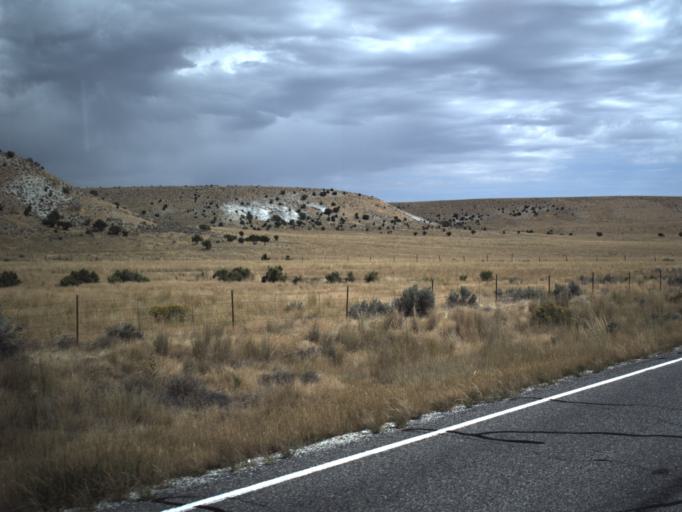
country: US
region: Idaho
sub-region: Cassia County
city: Burley
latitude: 41.8162
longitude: -113.2346
